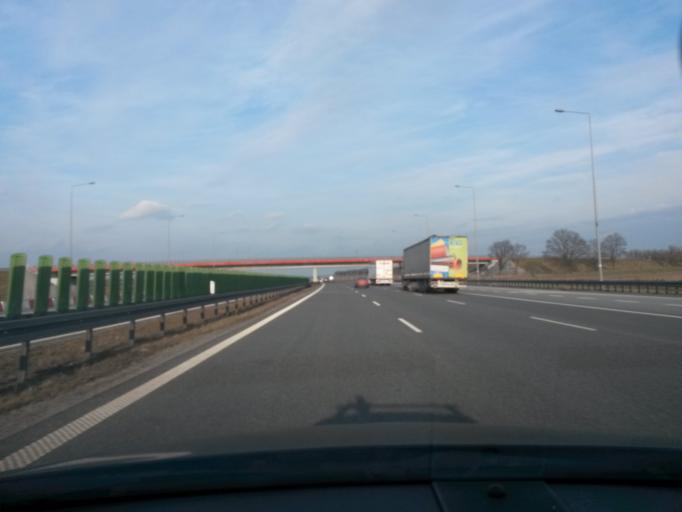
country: PL
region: Lodz Voivodeship
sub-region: Powiat zgierski
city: Strykow
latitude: 51.8927
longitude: 19.6481
